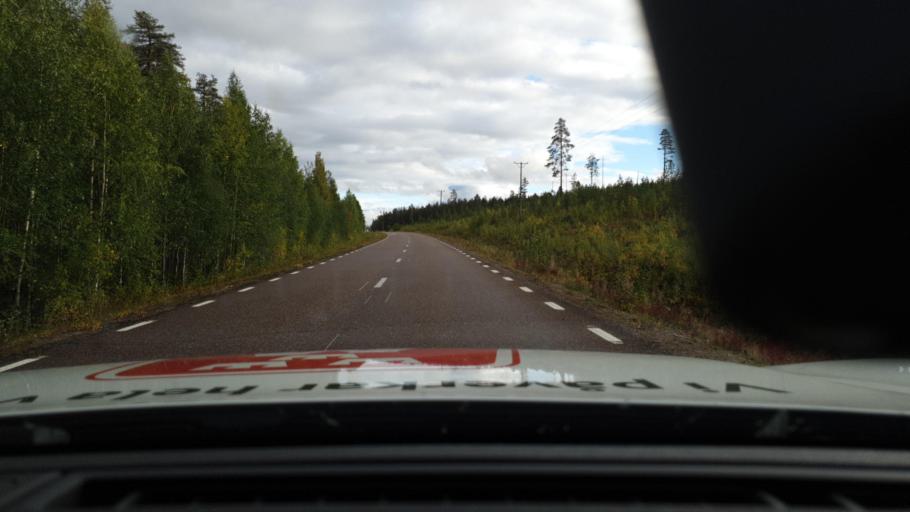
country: SE
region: Norrbotten
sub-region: Overkalix Kommun
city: OEverkalix
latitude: 67.0344
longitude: 22.5047
